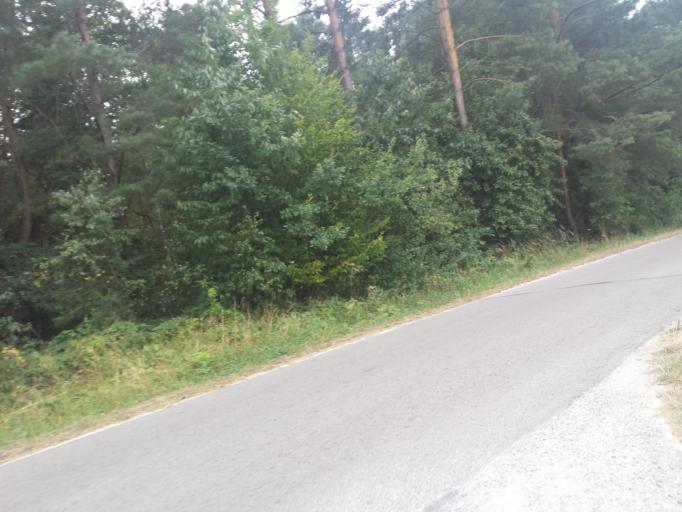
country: PL
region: Swietokrzyskie
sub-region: Powiat staszowski
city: Bogoria
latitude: 50.6555
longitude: 21.2249
